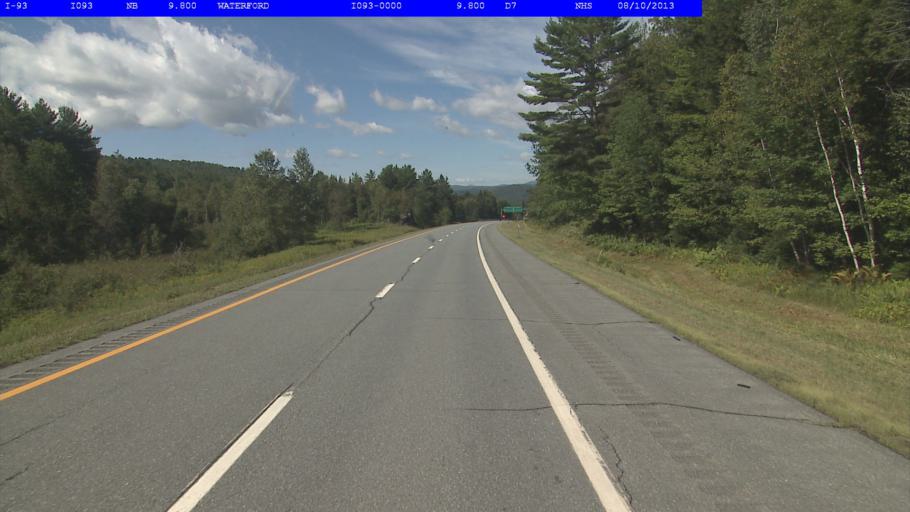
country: US
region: Vermont
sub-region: Caledonia County
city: Saint Johnsbury
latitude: 44.4083
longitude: -71.9931
